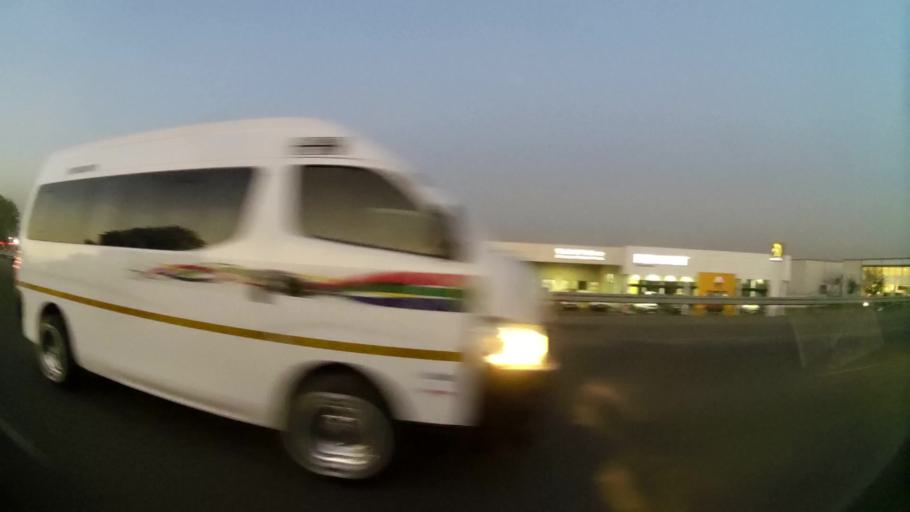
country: ZA
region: North-West
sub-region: Bojanala Platinum District Municipality
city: Rustenburg
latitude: -25.6900
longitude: 27.2535
